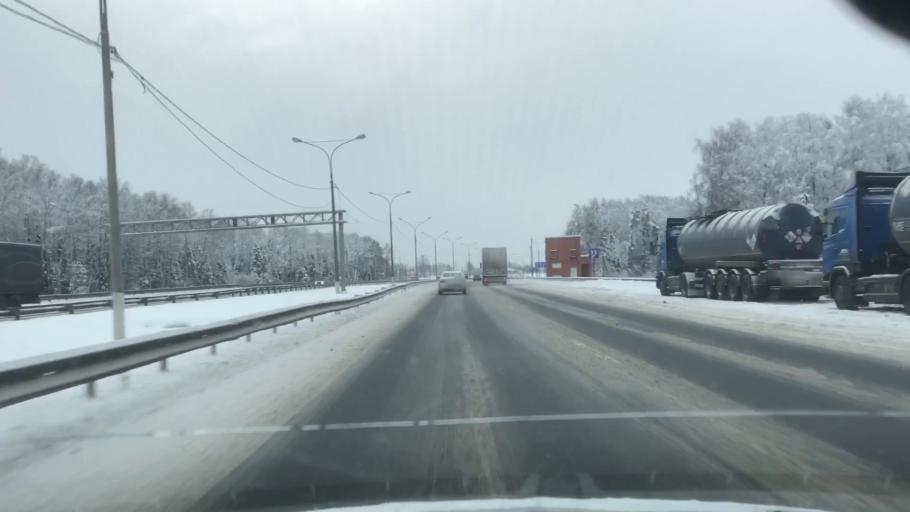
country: RU
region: Moskovskaya
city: Mikhnevo
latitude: 55.1319
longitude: 37.9344
